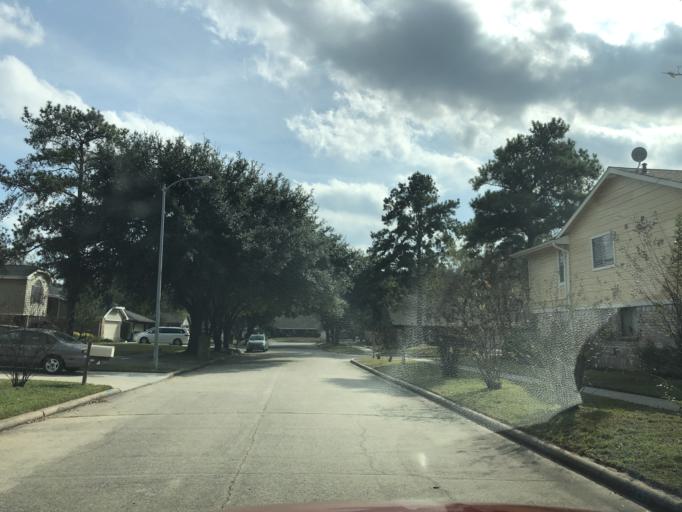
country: US
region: Texas
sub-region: Harris County
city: Tomball
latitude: 30.0389
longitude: -95.5424
